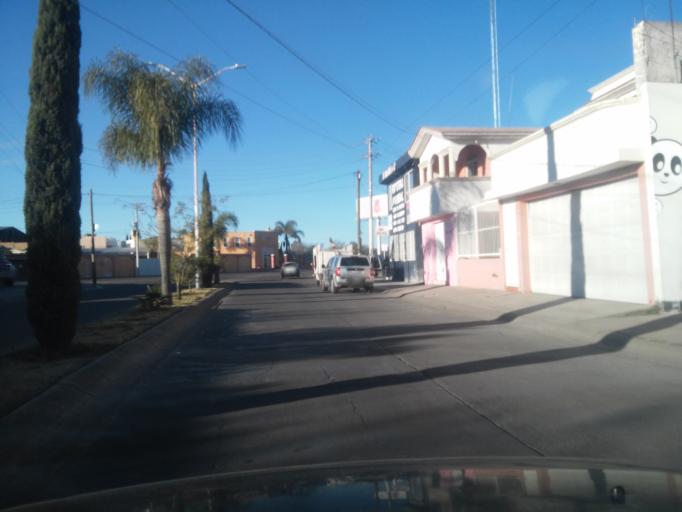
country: MX
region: Durango
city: Victoria de Durango
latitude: 24.0017
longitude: -104.6412
